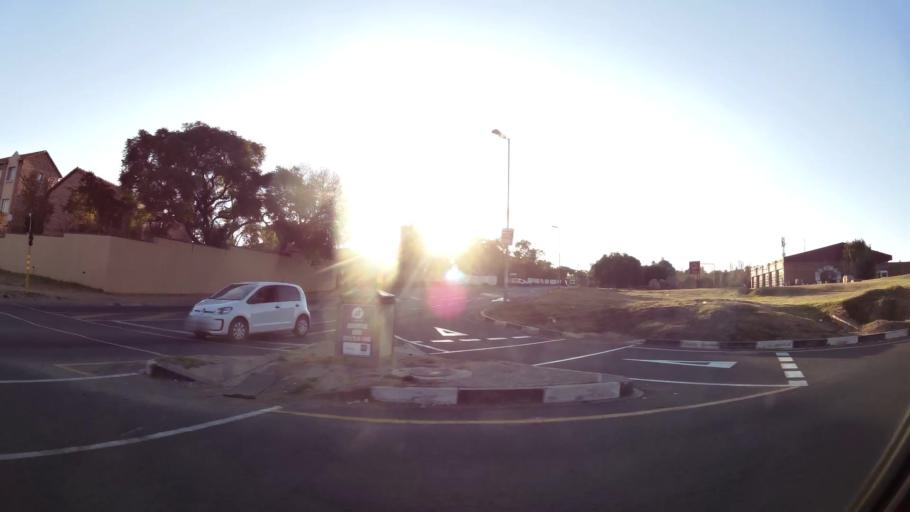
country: ZA
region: Gauteng
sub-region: City of Johannesburg Metropolitan Municipality
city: Midrand
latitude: -25.9908
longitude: 28.1209
